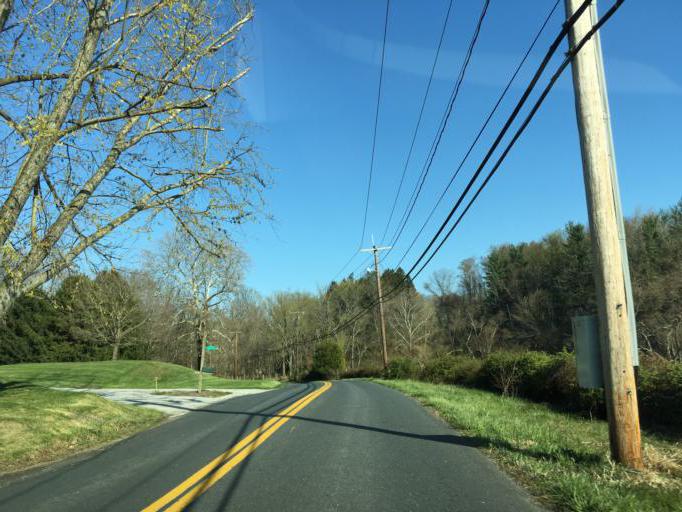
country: US
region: Maryland
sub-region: Baltimore County
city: Perry Hall
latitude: 39.4703
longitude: -76.4942
